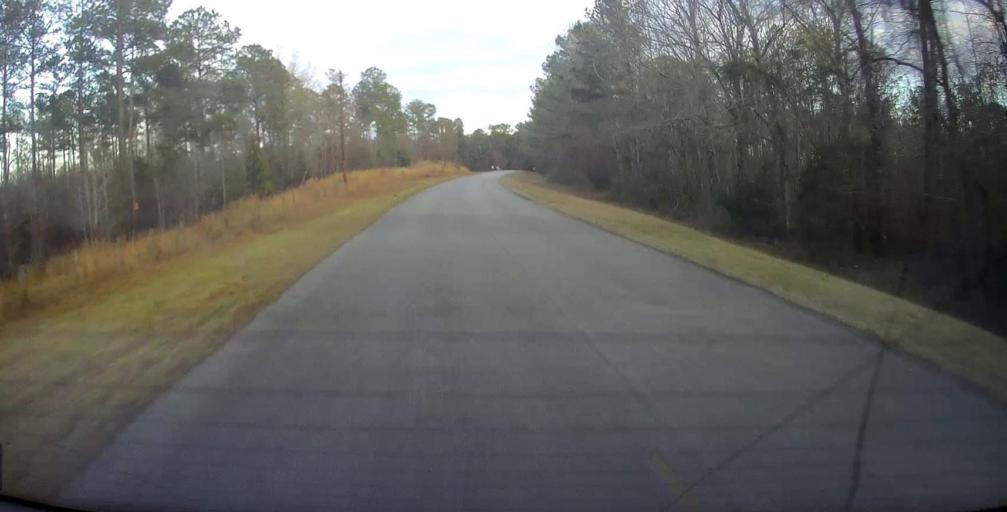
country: US
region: Georgia
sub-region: Harris County
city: Hamilton
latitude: 32.6156
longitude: -84.8242
